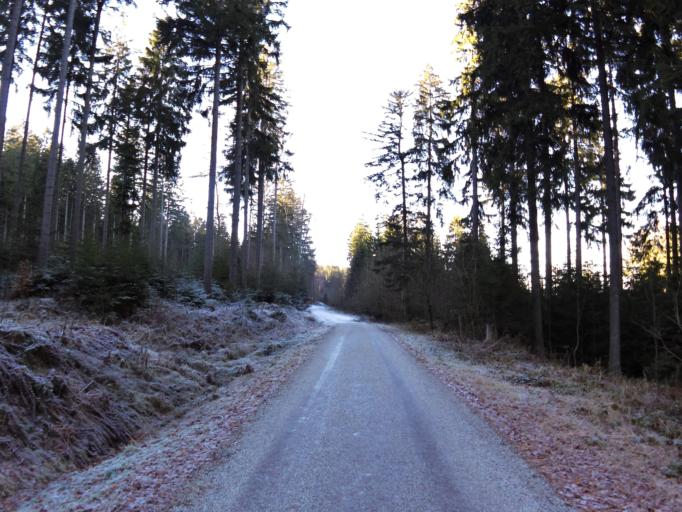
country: DE
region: Bavaria
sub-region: Upper Franconia
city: Bischofsgrun
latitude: 50.0463
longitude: 11.8171
